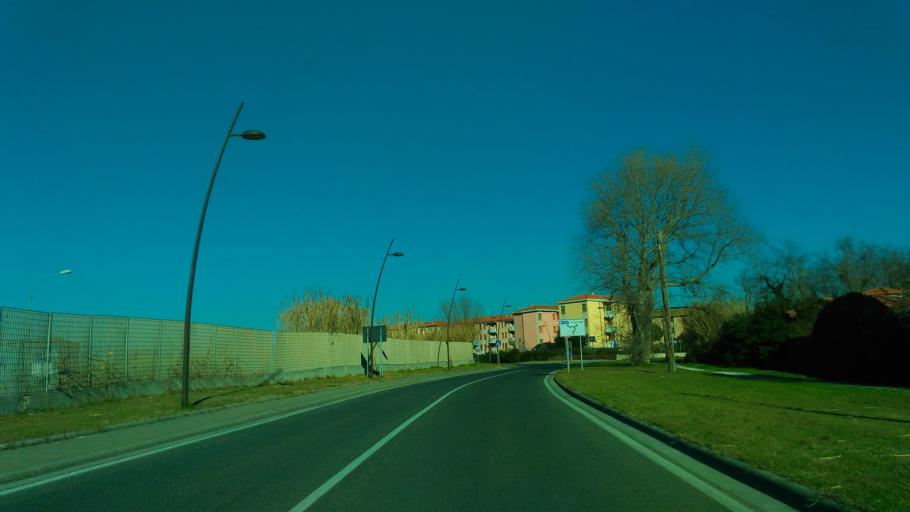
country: IT
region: Tuscany
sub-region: Province of Pisa
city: Marina di Pisa
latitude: 43.6764
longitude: 10.2762
